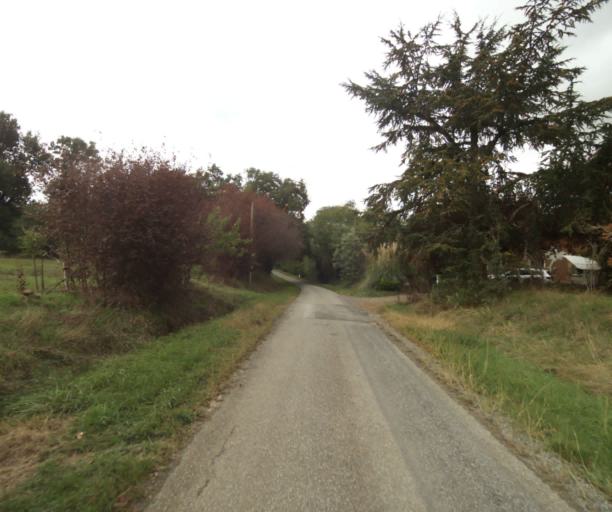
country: FR
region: Midi-Pyrenees
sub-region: Departement du Tarn-et-Garonne
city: Beaumont-de-Lomagne
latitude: 43.8978
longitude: 1.0966
